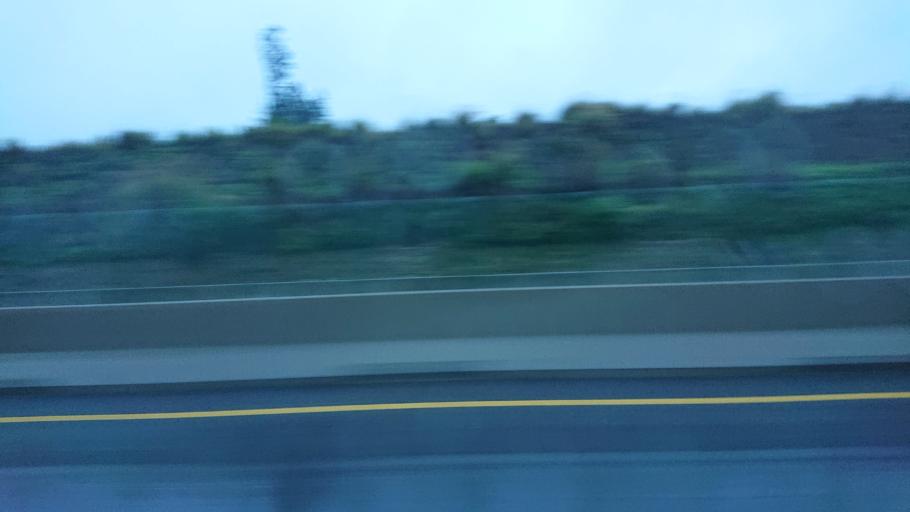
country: TW
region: Taiwan
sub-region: Miaoli
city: Miaoli
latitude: 24.5624
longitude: 120.7148
